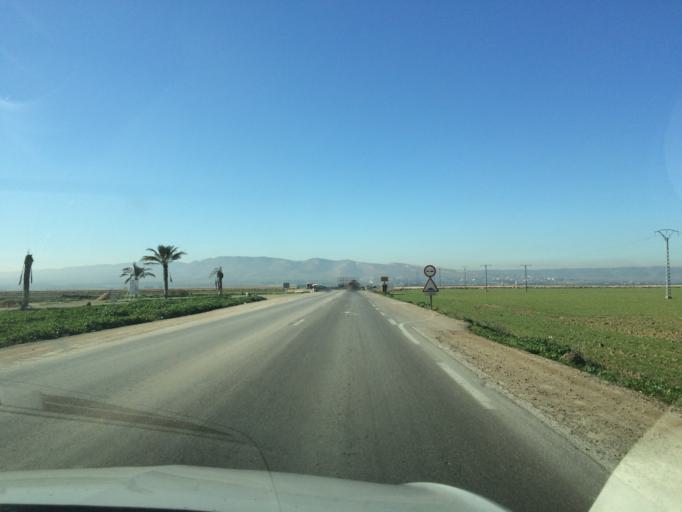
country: DZ
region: Relizane
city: Relizane
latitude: 35.8979
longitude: 0.5666
